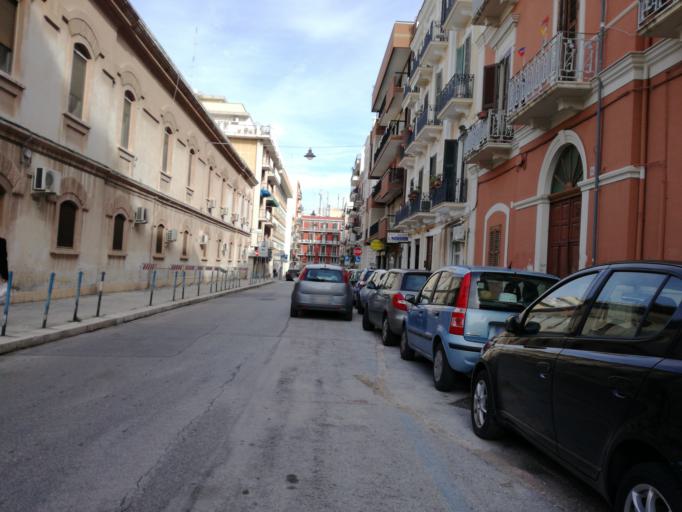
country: IT
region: Apulia
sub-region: Provincia di Bari
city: Bari
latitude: 41.1188
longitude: 16.8774
